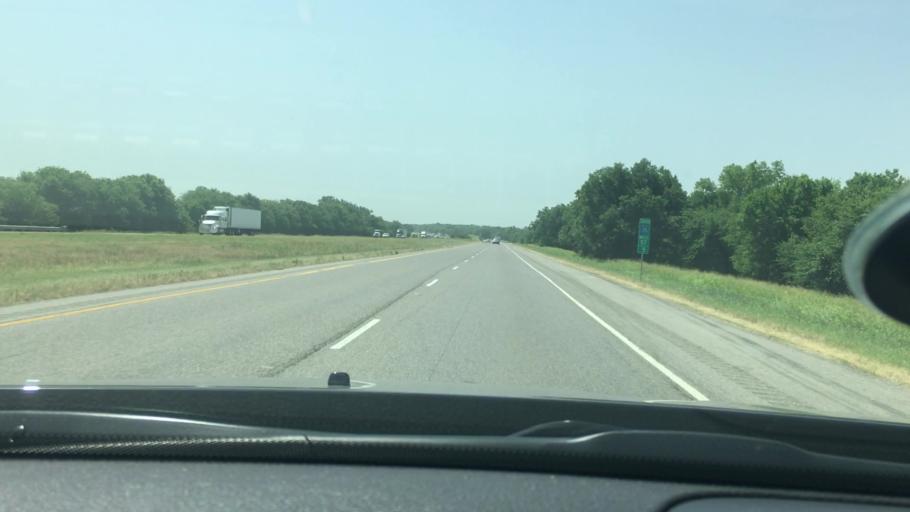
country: US
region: Oklahoma
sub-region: Murray County
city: Davis
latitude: 34.5315
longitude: -97.1871
